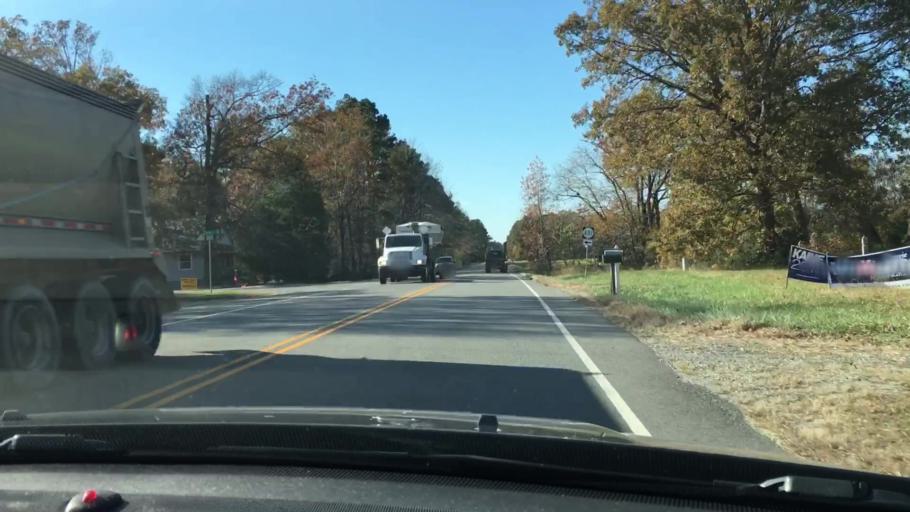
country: US
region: Virginia
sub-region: Hanover County
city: Hanover
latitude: 37.8135
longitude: -77.3014
